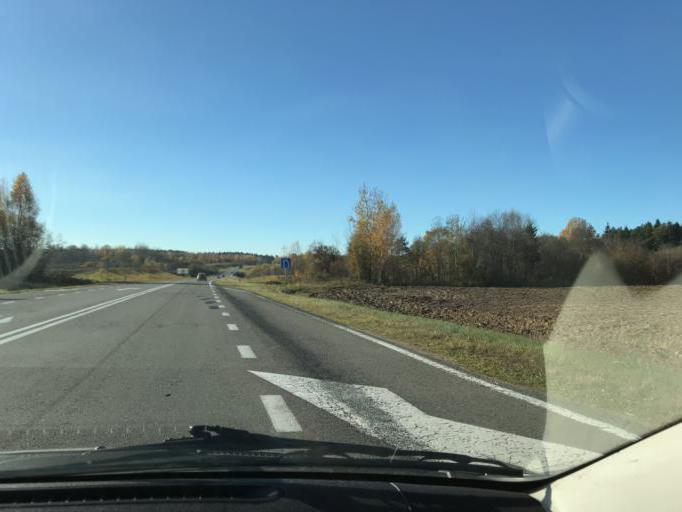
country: BY
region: Vitebsk
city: Syanno
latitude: 55.0500
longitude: 29.5192
